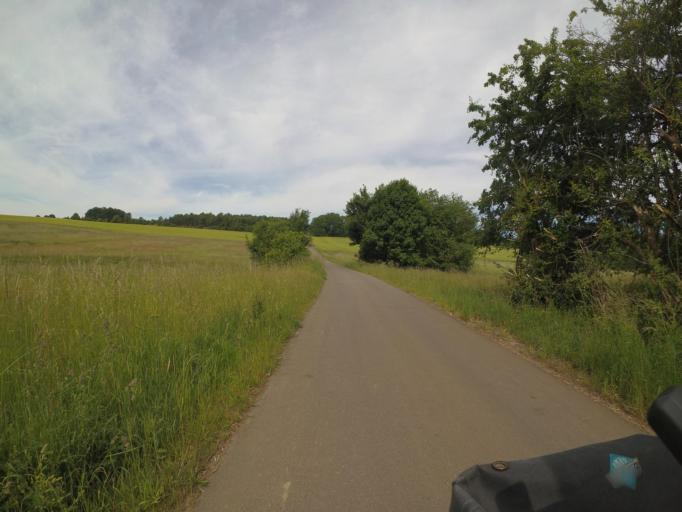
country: DE
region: Rheinland-Pfalz
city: Damflos
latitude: 49.6795
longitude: 6.9618
